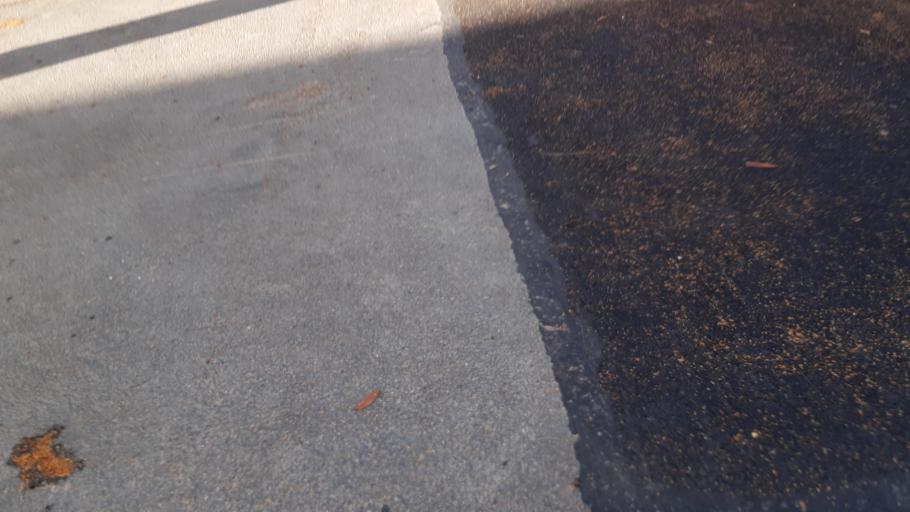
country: SE
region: Vaestra Goetaland
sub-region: Goteborg
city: Eriksbo
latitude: 57.7194
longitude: 12.0301
